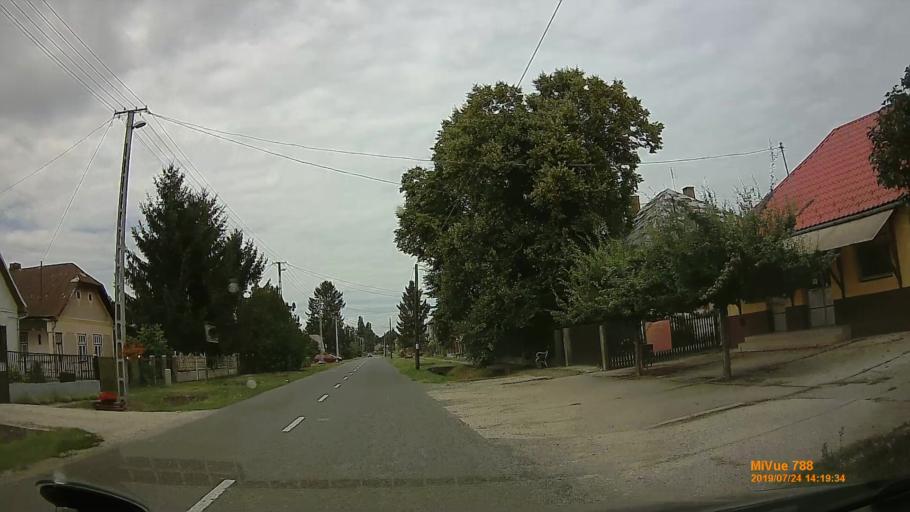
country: HU
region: Szabolcs-Szatmar-Bereg
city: Mandok
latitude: 48.3196
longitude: 22.2694
